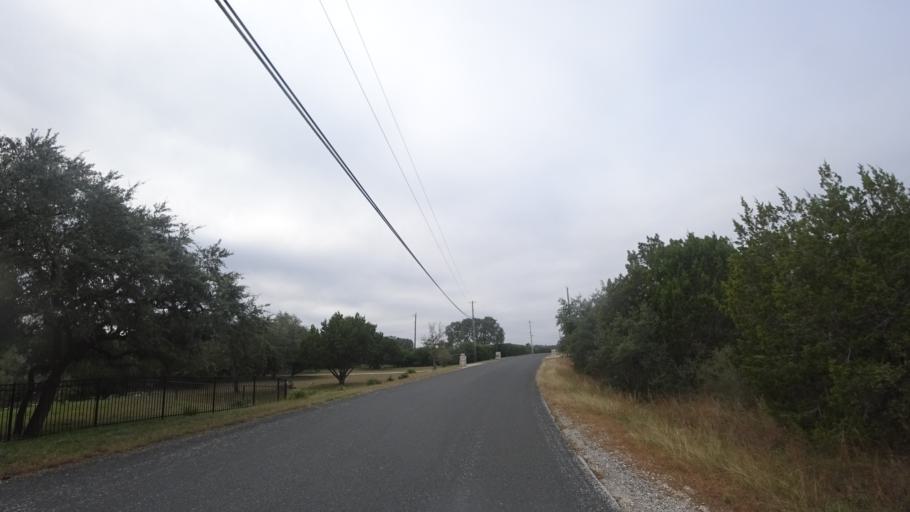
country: US
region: Texas
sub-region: Travis County
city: Hudson Bend
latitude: 30.3913
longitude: -97.9149
